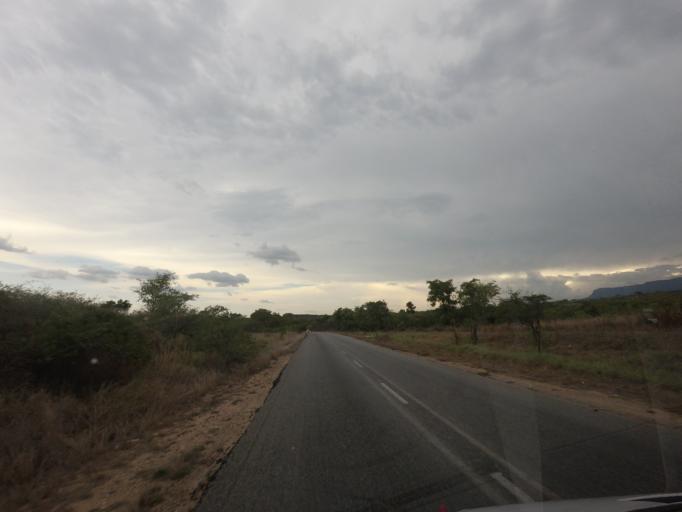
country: ZA
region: Limpopo
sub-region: Mopani District Municipality
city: Hoedspruit
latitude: -24.5250
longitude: 30.9649
